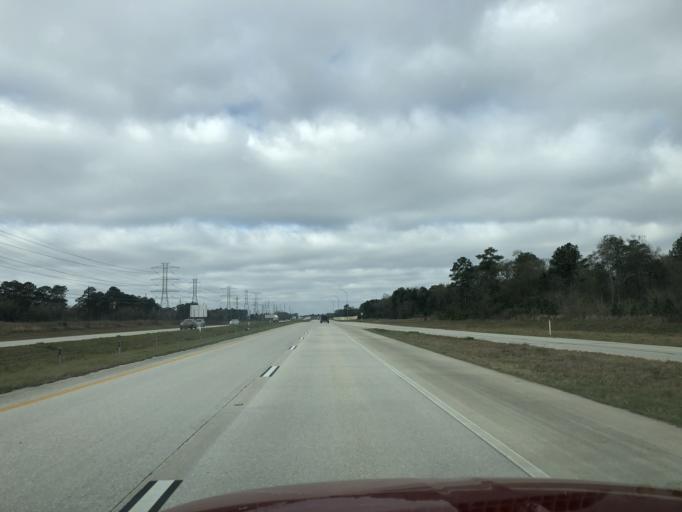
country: US
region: Texas
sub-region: Harris County
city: Spring
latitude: 30.0908
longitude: -95.4662
